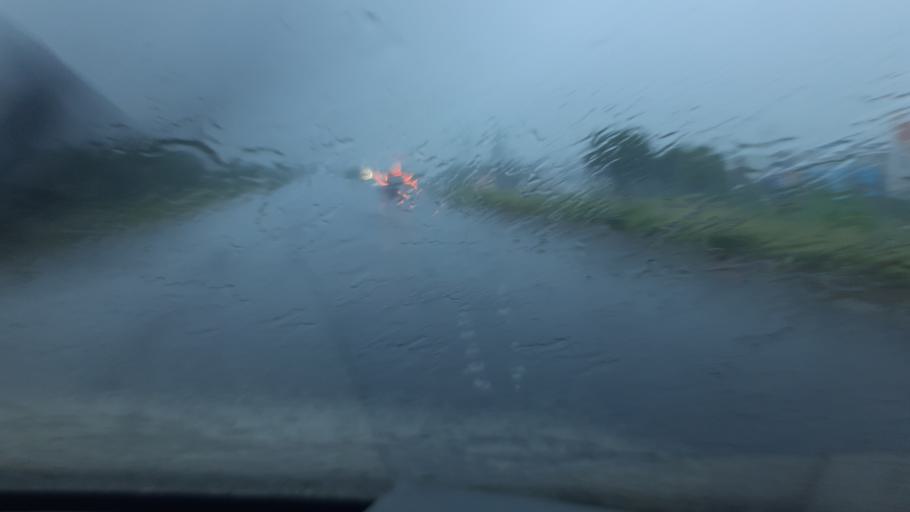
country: IN
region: Tamil Nadu
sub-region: Virudhunagar
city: Virudunagar
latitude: 9.5070
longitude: 77.9414
